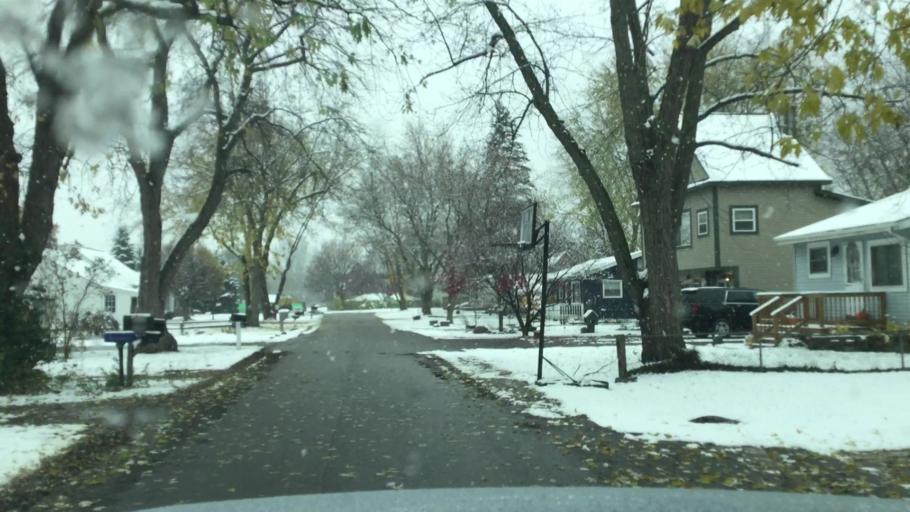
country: US
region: Michigan
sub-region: Oakland County
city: Oxford
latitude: 42.8103
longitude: -83.2951
